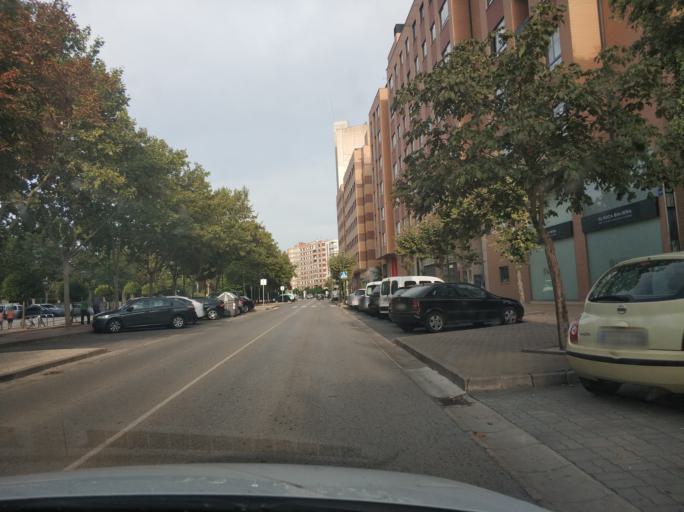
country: ES
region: Castille and Leon
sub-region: Provincia de Burgos
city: Burgos
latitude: 42.3486
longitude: -3.6800
